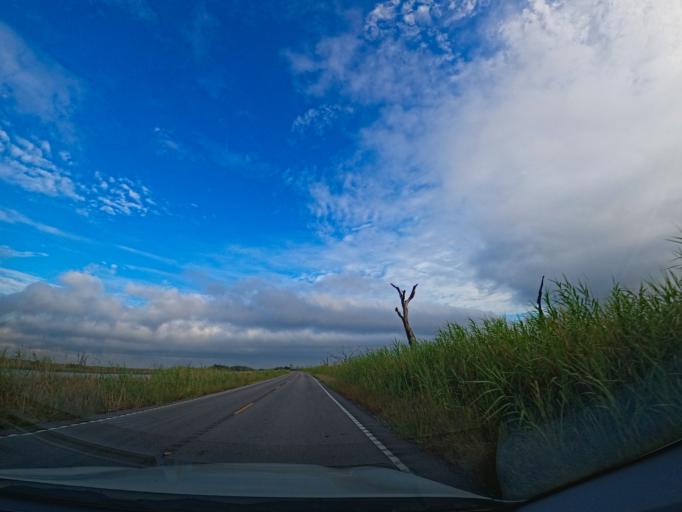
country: US
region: Louisiana
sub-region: Terrebonne Parish
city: Dulac
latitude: 29.3374
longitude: -90.6922
